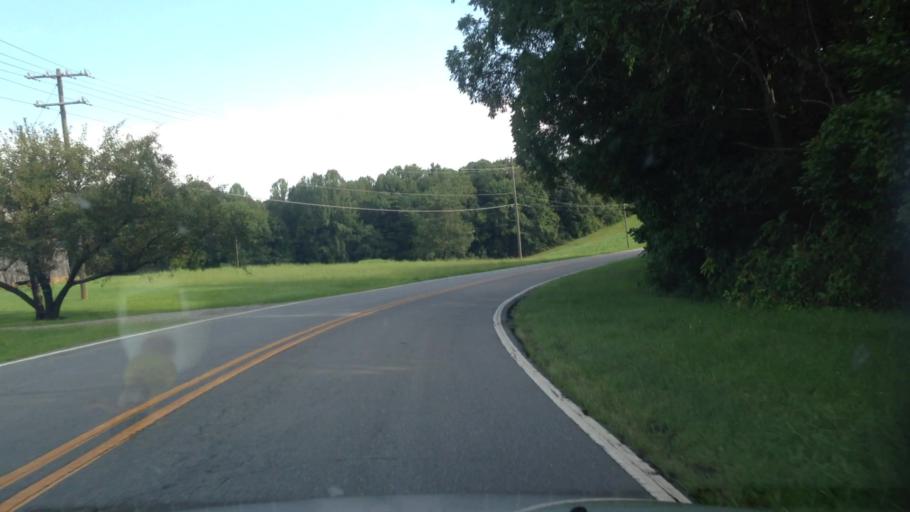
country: US
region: North Carolina
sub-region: Guilford County
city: Oak Ridge
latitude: 36.1963
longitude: -80.0610
